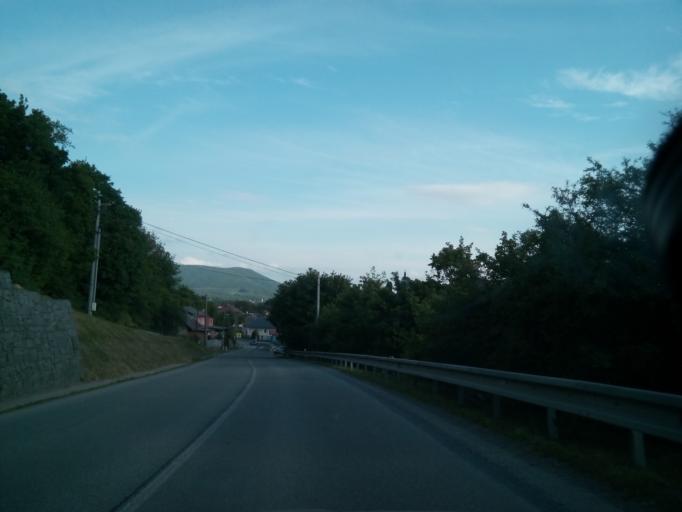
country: SK
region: Kosicky
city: Kosice
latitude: 48.7935
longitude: 21.2430
